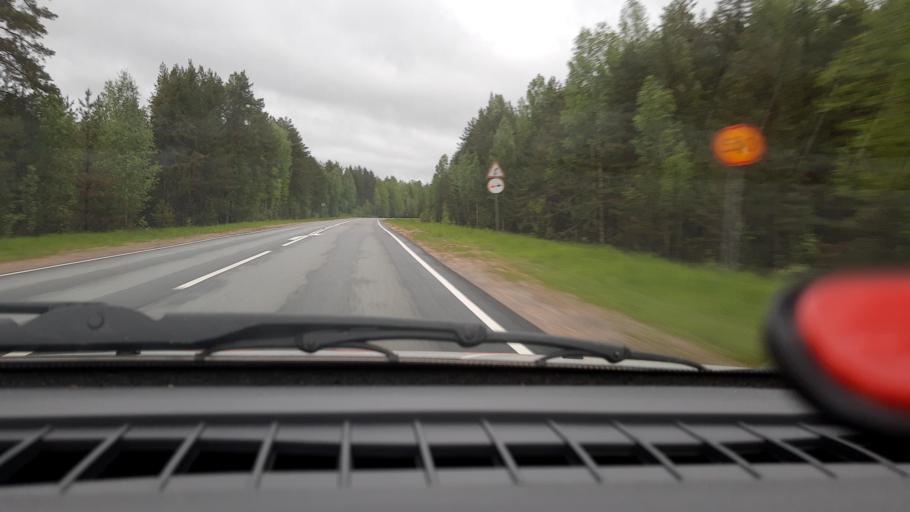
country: RU
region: Nizjnij Novgorod
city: Krasnyye Baki
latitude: 57.2094
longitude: 45.4619
